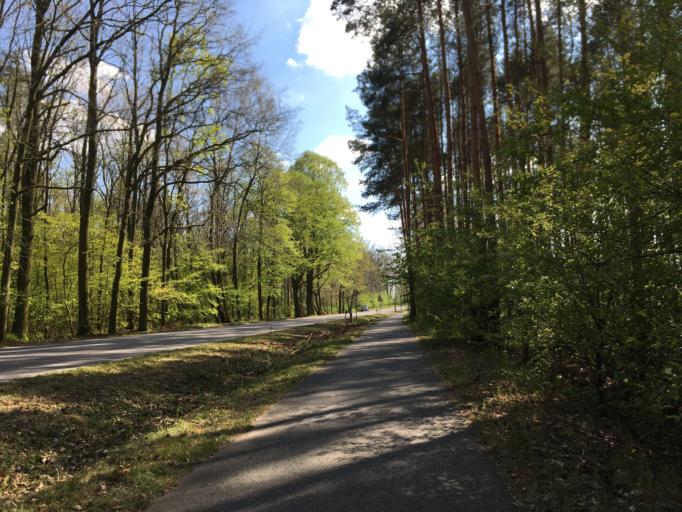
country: DE
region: Brandenburg
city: Ahrensfelde
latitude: 52.5981
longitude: 13.5689
